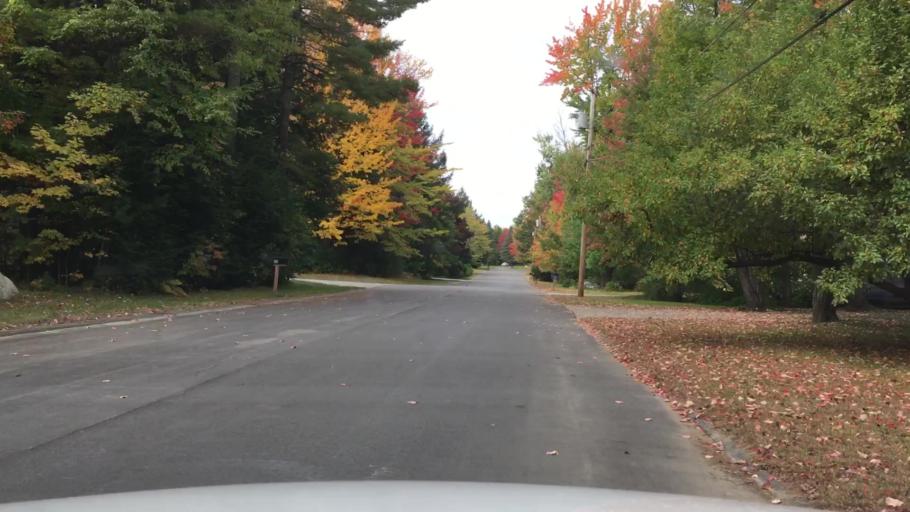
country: US
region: Maine
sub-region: Kennebec County
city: Oakland
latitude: 44.5460
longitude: -69.6870
